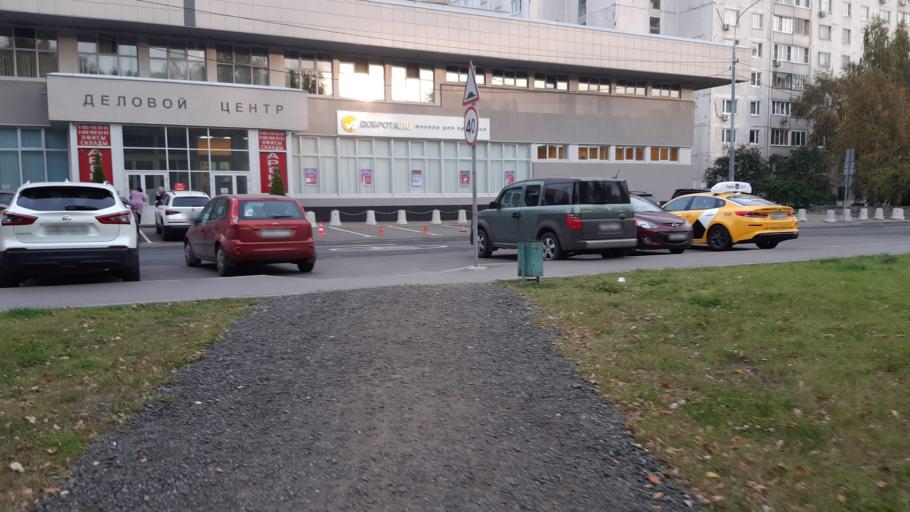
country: RU
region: Moscow
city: Vagonoremont
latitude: 55.9051
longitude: 37.5672
